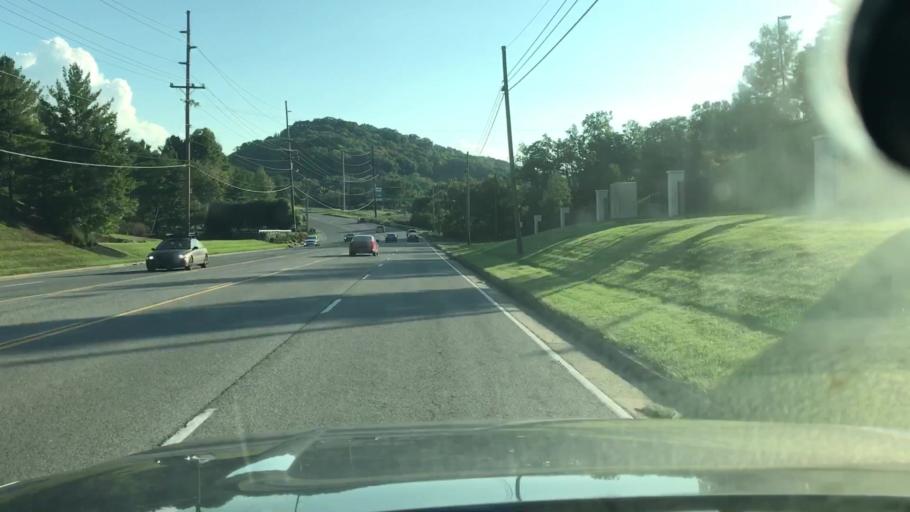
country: US
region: Tennessee
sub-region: Davidson County
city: Belle Meade
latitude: 36.1010
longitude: -86.9234
